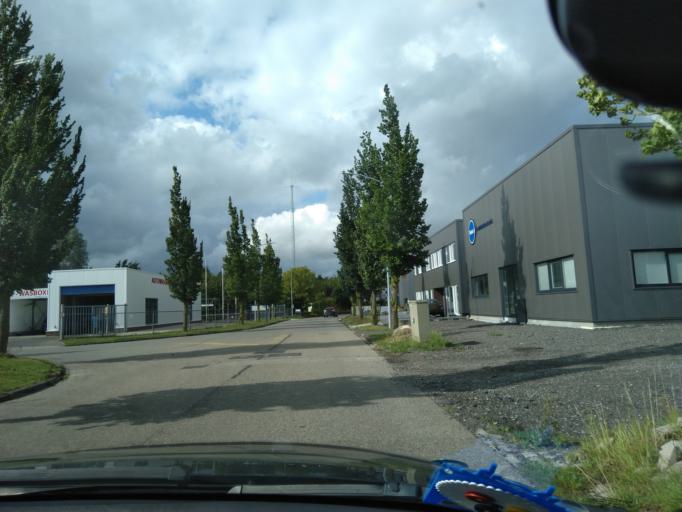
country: NL
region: Groningen
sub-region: Gemeente Zuidhorn
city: Noordhorn
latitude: 53.2555
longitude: 6.3958
